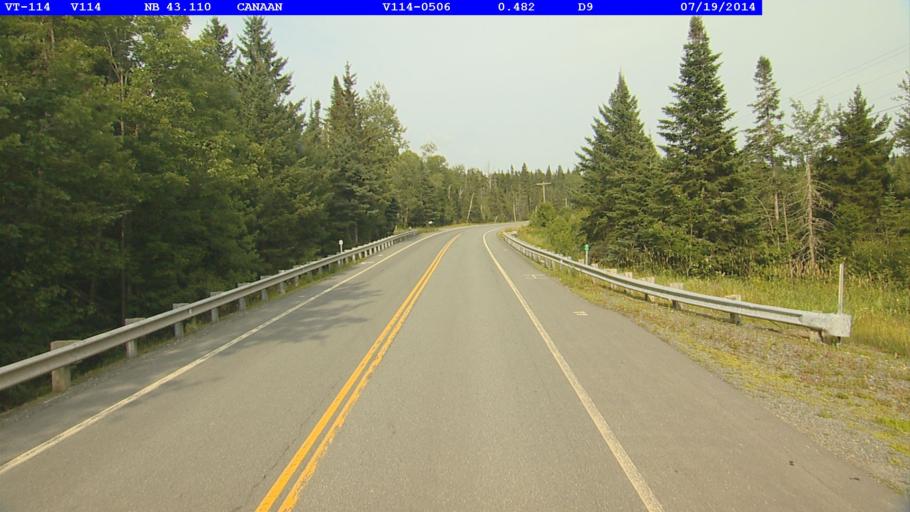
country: CA
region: Quebec
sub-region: Estrie
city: Coaticook
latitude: 45.0060
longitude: -71.6839
